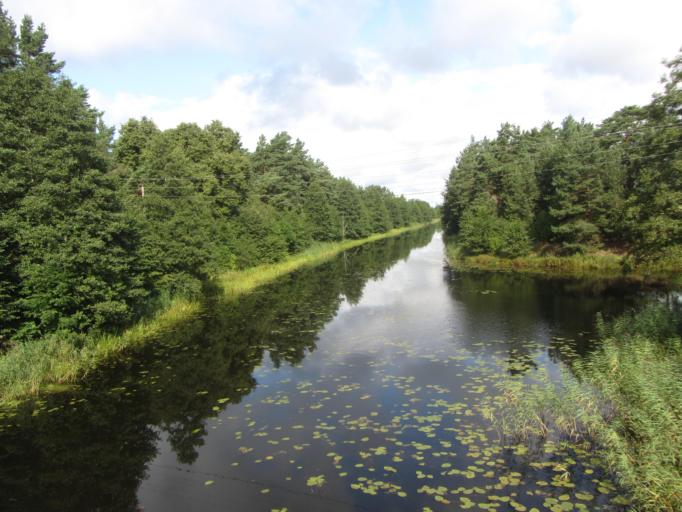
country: LT
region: Klaipedos apskritis
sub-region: Klaipeda
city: Klaipeda
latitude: 55.6133
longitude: 21.1913
